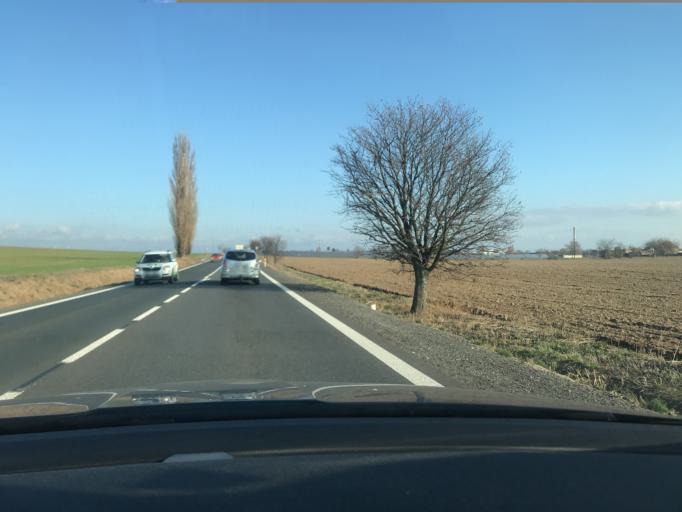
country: CZ
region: Kralovehradecky
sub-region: Okres Hradec Kralove
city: Smirice
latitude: 50.2936
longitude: 15.8385
